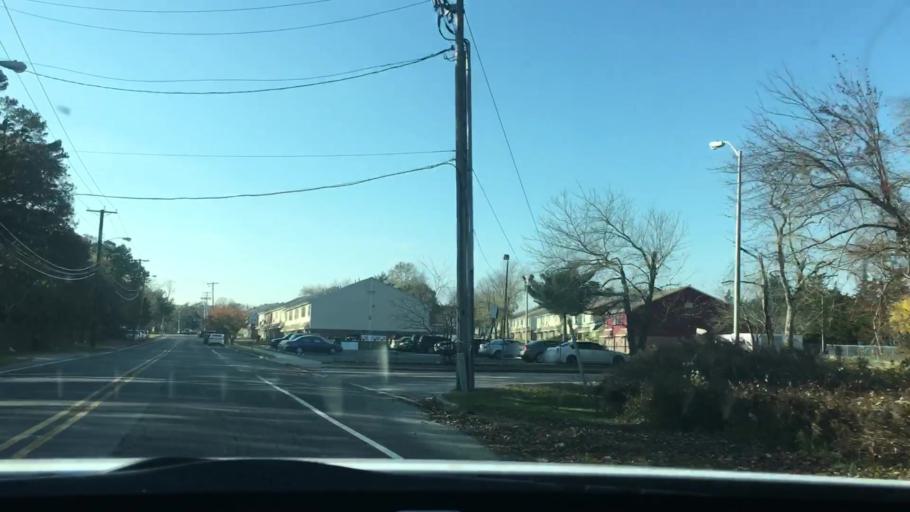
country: US
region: New Jersey
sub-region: Atlantic County
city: Absecon
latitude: 39.4144
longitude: -74.5083
